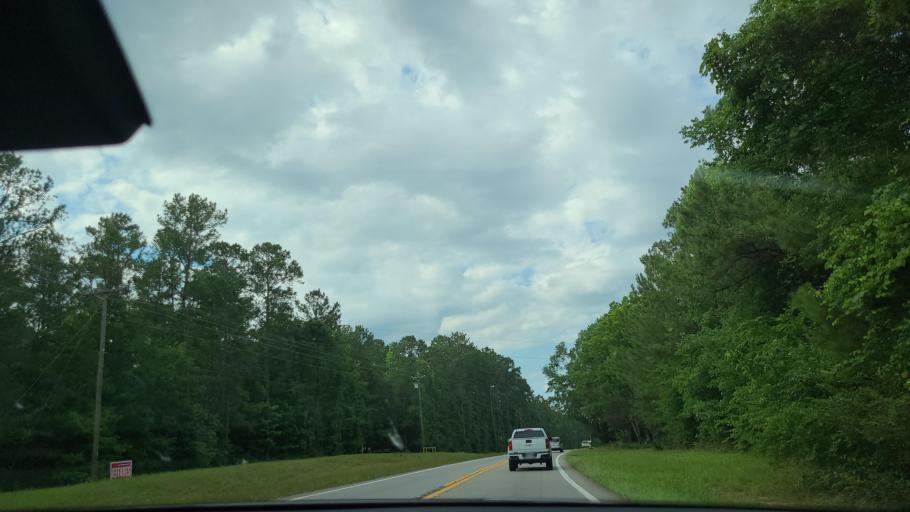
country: US
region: Georgia
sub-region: Putnam County
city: Eatonton
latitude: 33.1756
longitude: -83.4417
